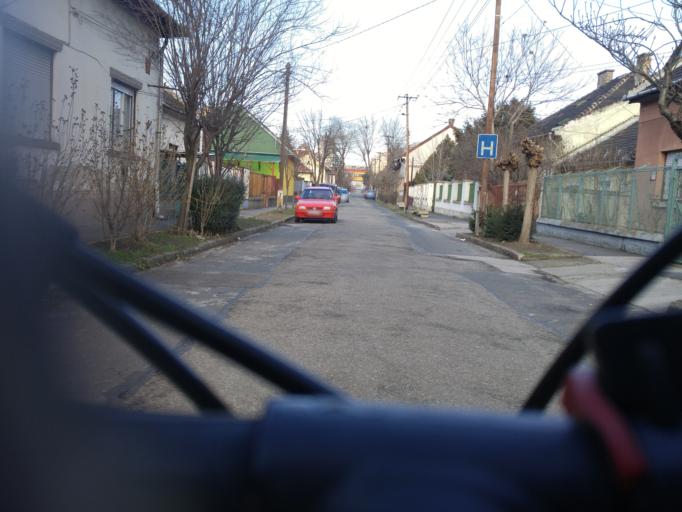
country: HU
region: Budapest
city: Budapest XX. keruelet
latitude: 47.4315
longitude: 19.1093
